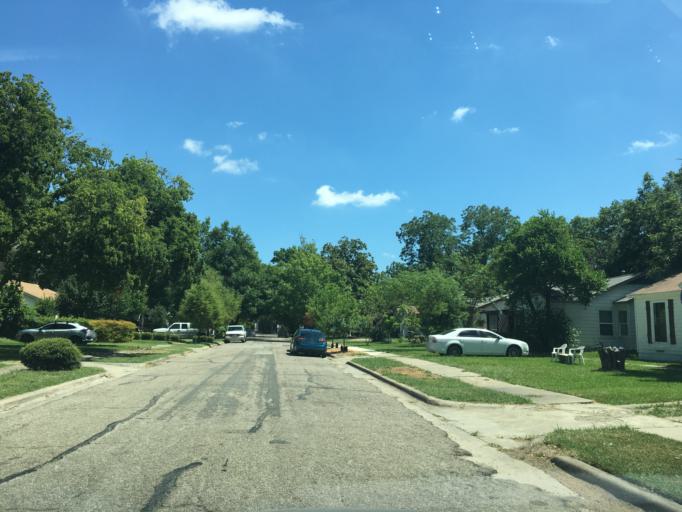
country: US
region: Texas
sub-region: Dallas County
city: Garland
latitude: 32.8414
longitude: -96.6871
